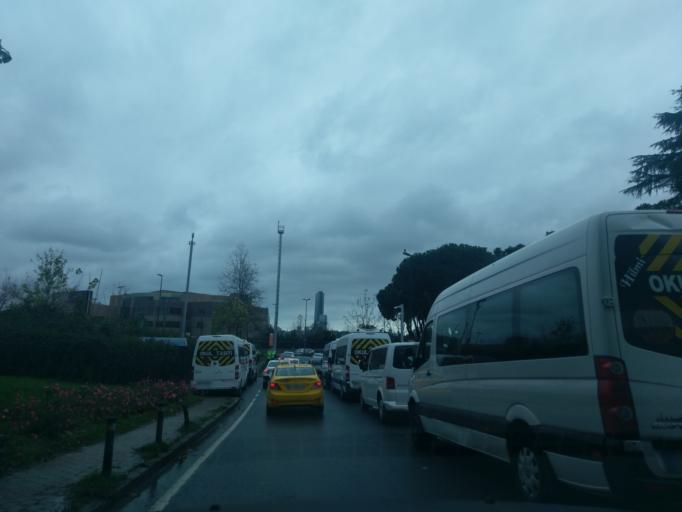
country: TR
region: Istanbul
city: Sisli
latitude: 41.1072
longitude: 29.0139
